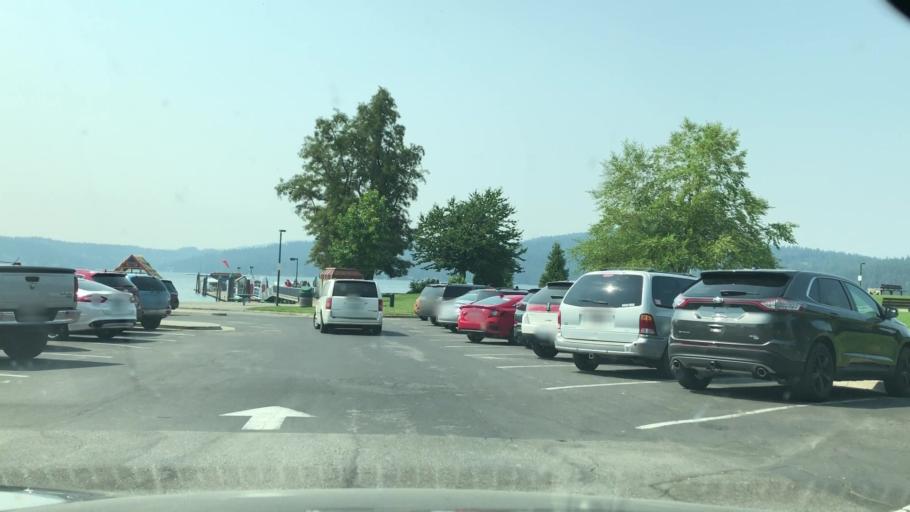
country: US
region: Idaho
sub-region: Kootenai County
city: Coeur d'Alene
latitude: 47.6739
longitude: -116.7868
